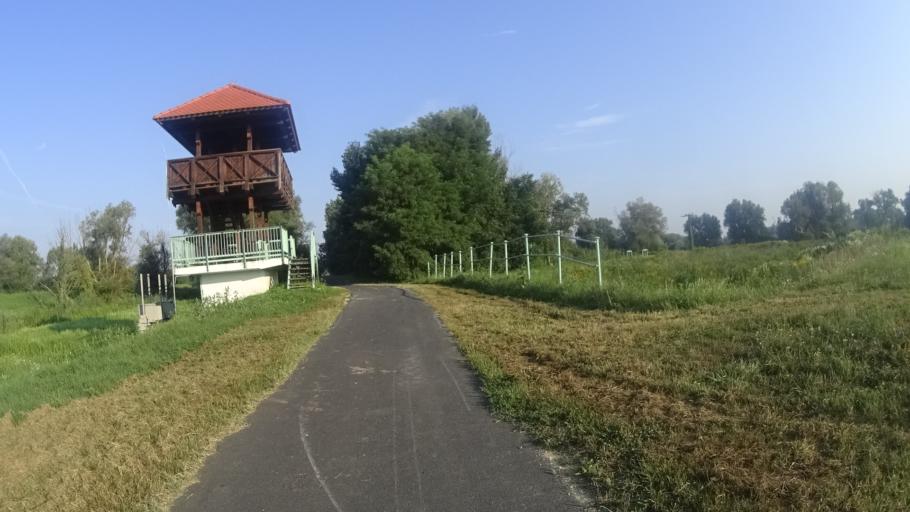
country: HU
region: Zala
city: Sarmellek
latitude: 46.6461
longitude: 17.1554
